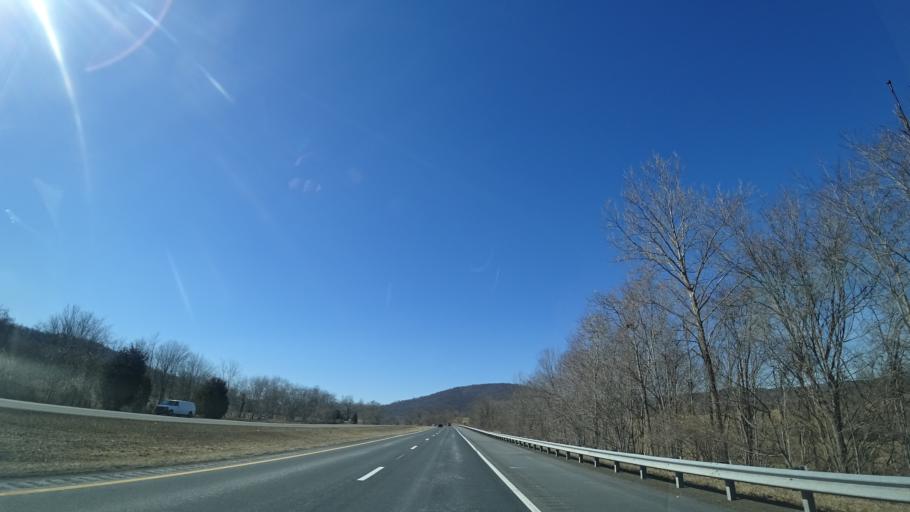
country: US
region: Virginia
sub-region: Fauquier County
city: Marshall
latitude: 38.9079
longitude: -77.9564
